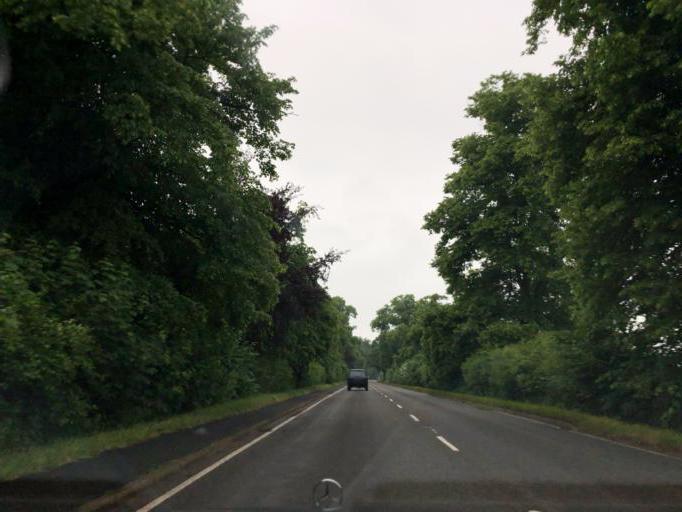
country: GB
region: England
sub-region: Warwickshire
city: Wroxall
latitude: 52.3043
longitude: -1.6555
